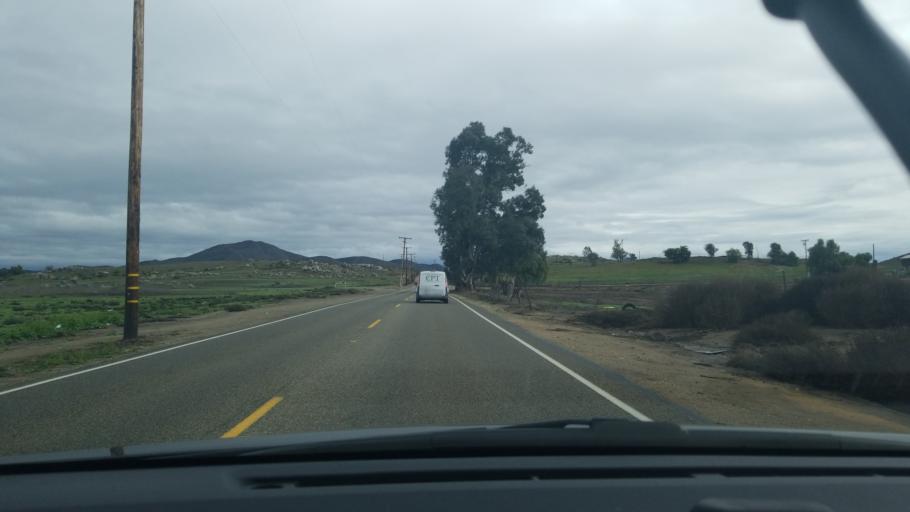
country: US
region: California
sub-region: Riverside County
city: Winchester
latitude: 33.6417
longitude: -117.0990
